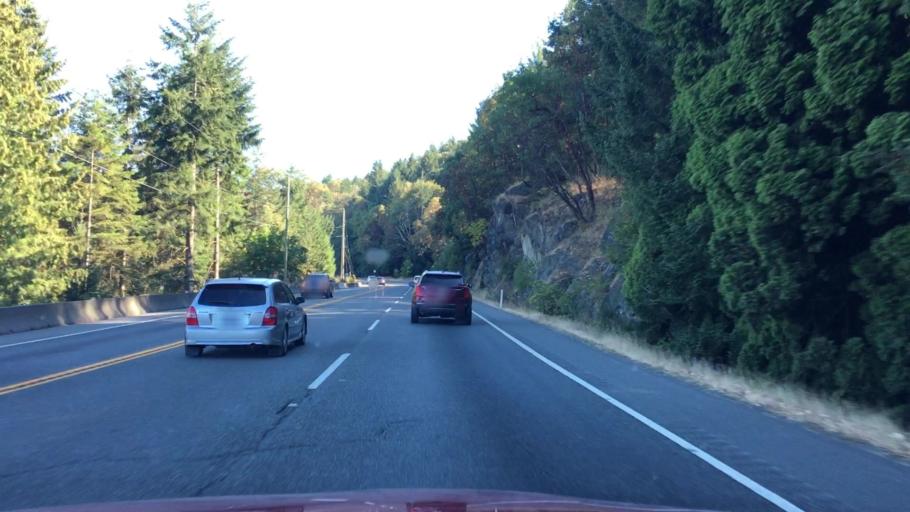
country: CA
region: British Columbia
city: North Saanich
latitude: 48.5906
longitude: -123.5319
